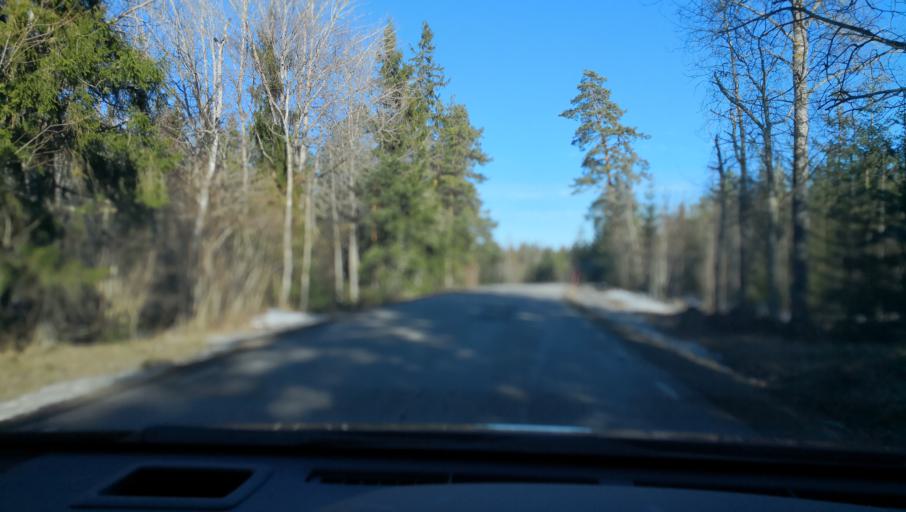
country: SE
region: Uppsala
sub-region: Osthammars Kommun
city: Osterbybruk
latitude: 60.2511
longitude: 17.9438
